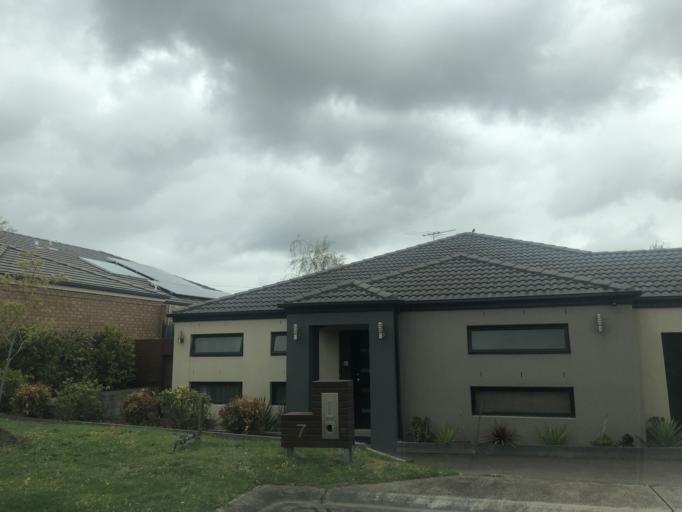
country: AU
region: Victoria
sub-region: Knox
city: Rowville
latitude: -37.9399
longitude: 145.2491
